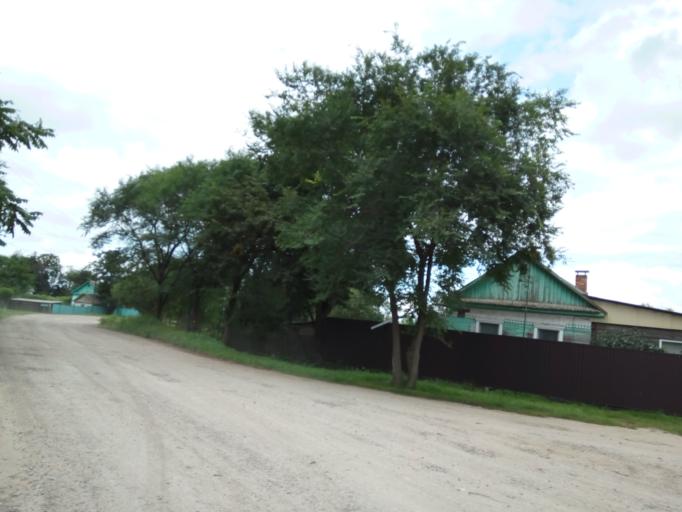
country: RU
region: Primorskiy
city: Dal'nerechensk
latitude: 45.9351
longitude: 133.8147
